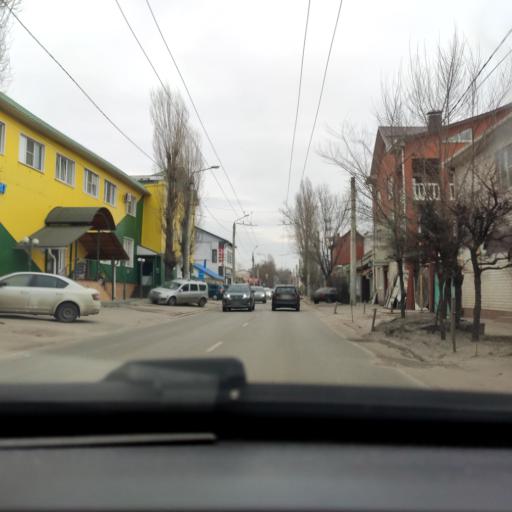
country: RU
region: Voronezj
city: Shilovo
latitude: 51.4435
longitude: 39.0962
